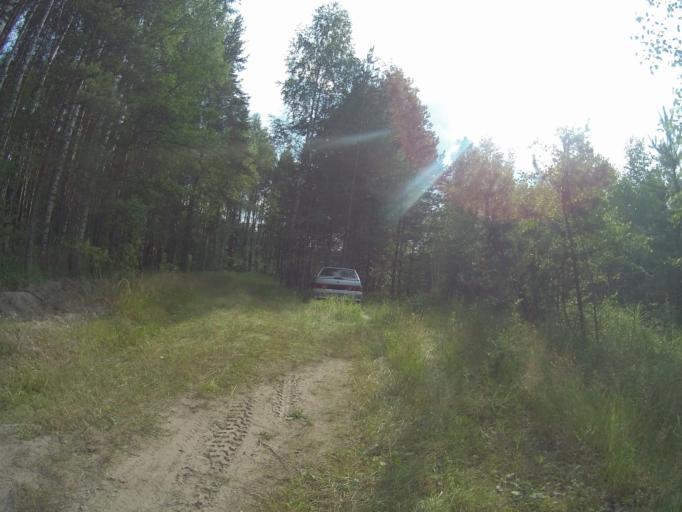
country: RU
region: Vladimir
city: Vorsha
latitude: 56.0003
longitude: 40.1254
